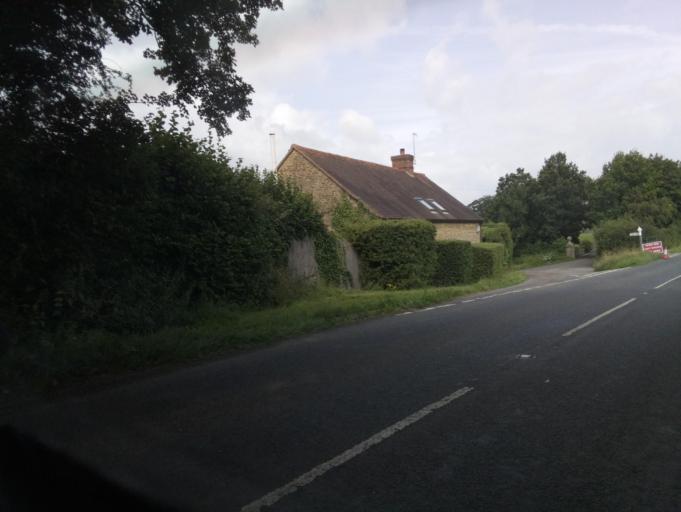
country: GB
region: England
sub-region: Somerset
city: Redlynch
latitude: 51.0875
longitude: -2.4140
